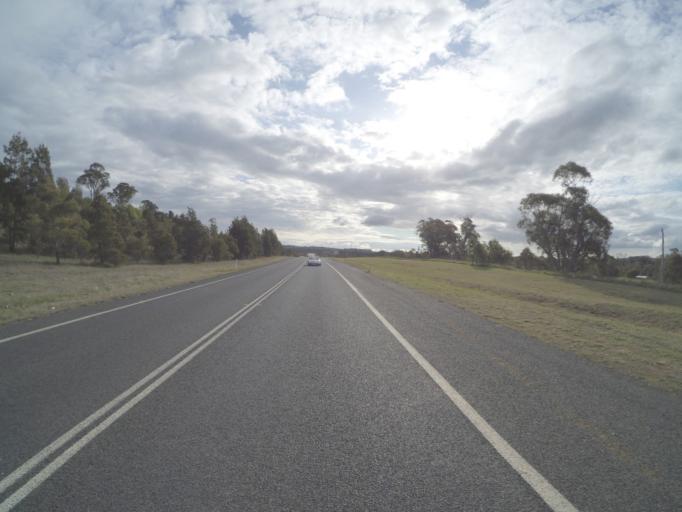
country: AU
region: New South Wales
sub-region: Wingecarribee
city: Bundanoon
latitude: -34.5859
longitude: 150.2604
